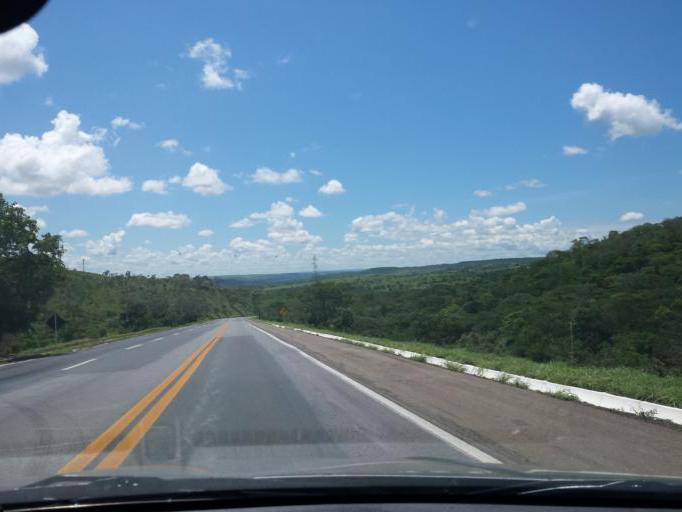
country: BR
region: Goias
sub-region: Luziania
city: Luziania
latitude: -16.3786
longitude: -47.8295
